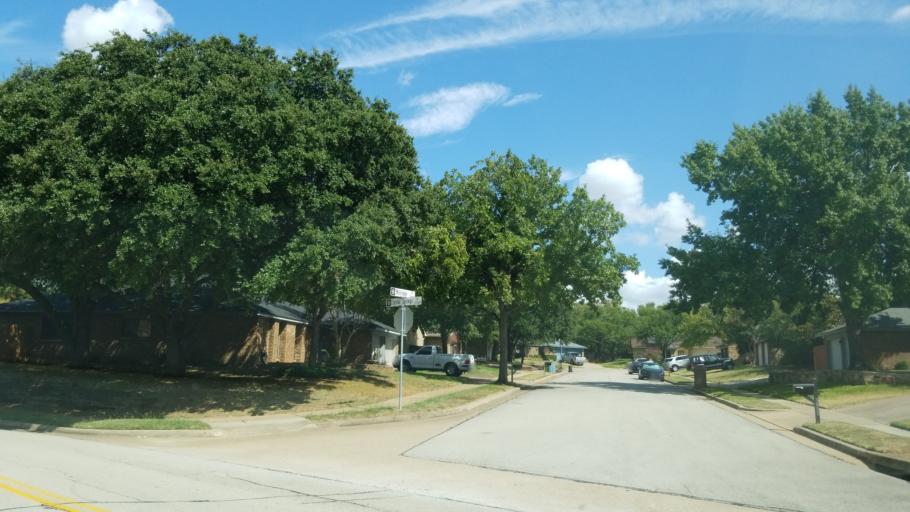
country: US
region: Texas
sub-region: Tarrant County
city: Euless
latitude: 32.8590
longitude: -97.1100
